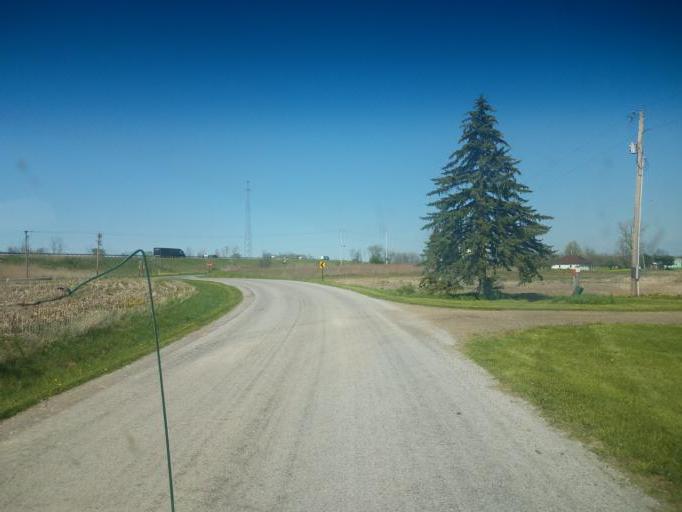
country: US
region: Ohio
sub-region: Medina County
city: Lodi
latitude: 40.9858
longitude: -82.0348
